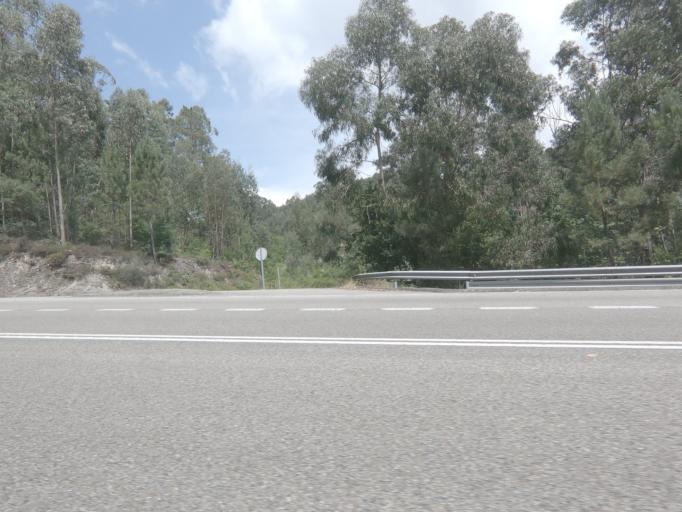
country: ES
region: Galicia
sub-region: Provincia de Pontevedra
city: Tomino
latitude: 42.0459
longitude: -8.7280
